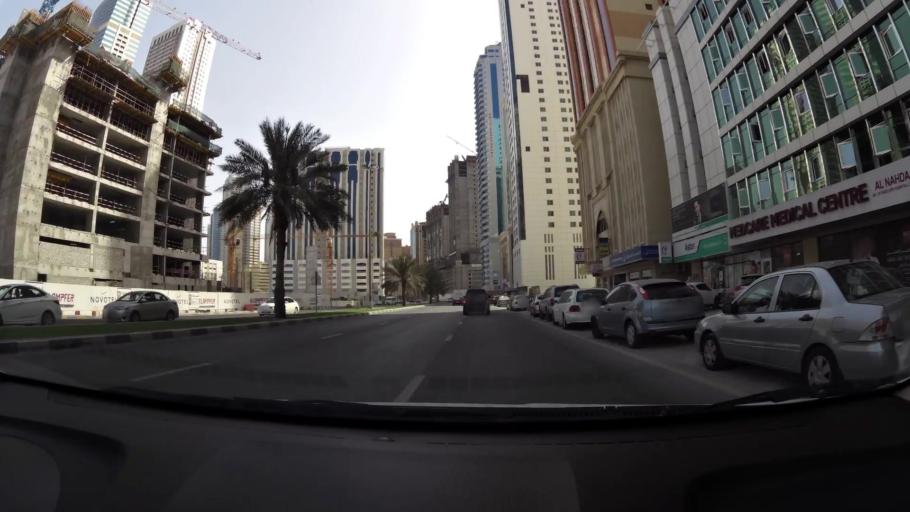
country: AE
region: Ash Shariqah
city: Sharjah
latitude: 25.3113
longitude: 55.3736
